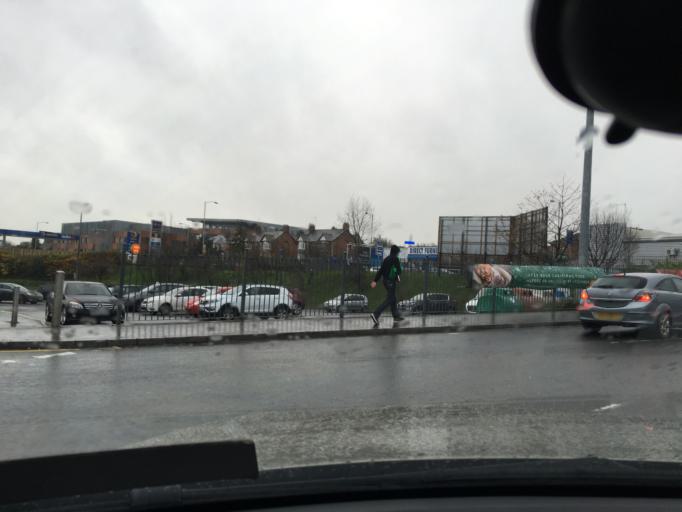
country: GB
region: Northern Ireland
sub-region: City of Belfast
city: Belfast
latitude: 54.5807
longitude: -5.9795
